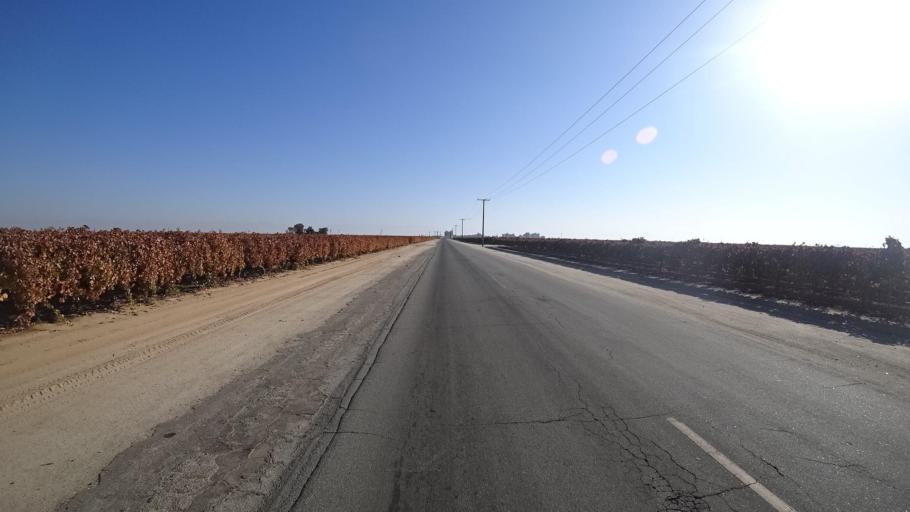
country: US
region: California
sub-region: Kern County
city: Delano
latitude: 35.7469
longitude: -119.1928
